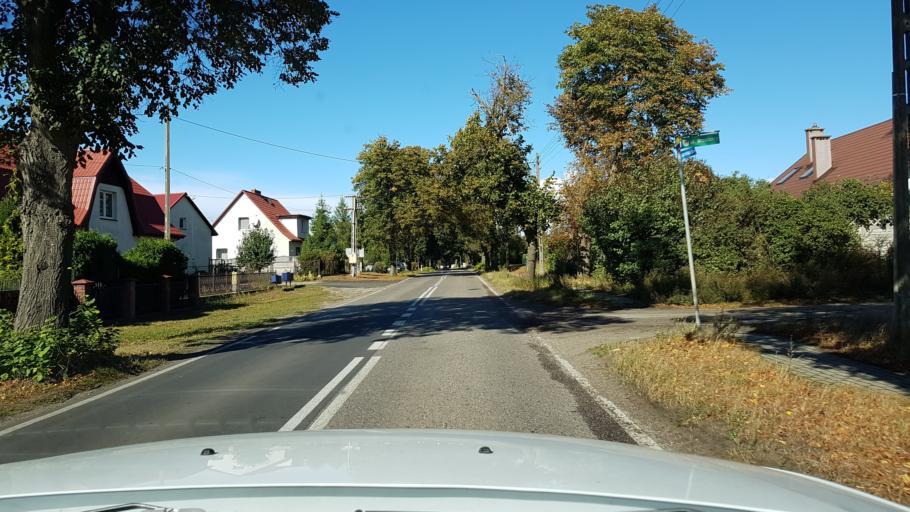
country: PL
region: West Pomeranian Voivodeship
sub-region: Powiat gryfinski
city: Gryfino
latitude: 53.2065
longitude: 14.5016
